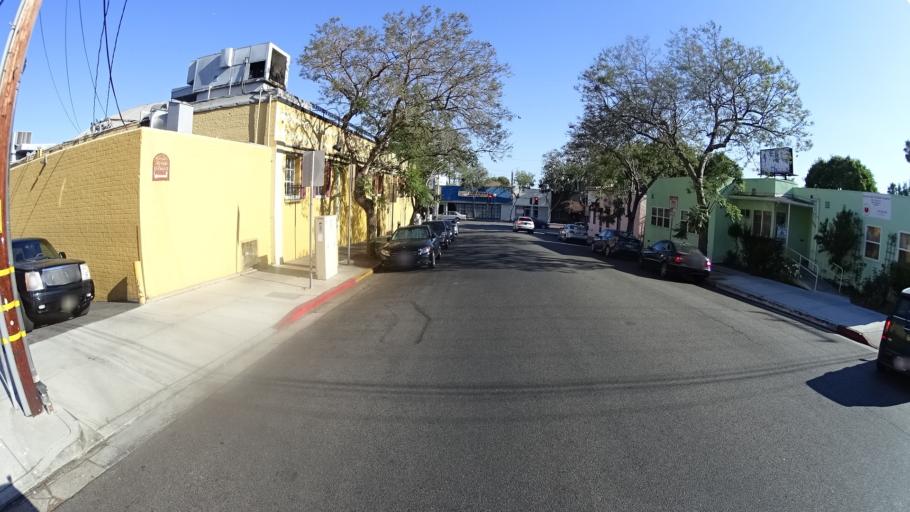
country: US
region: California
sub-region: Los Angeles County
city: West Hollywood
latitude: 34.0913
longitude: -118.3645
